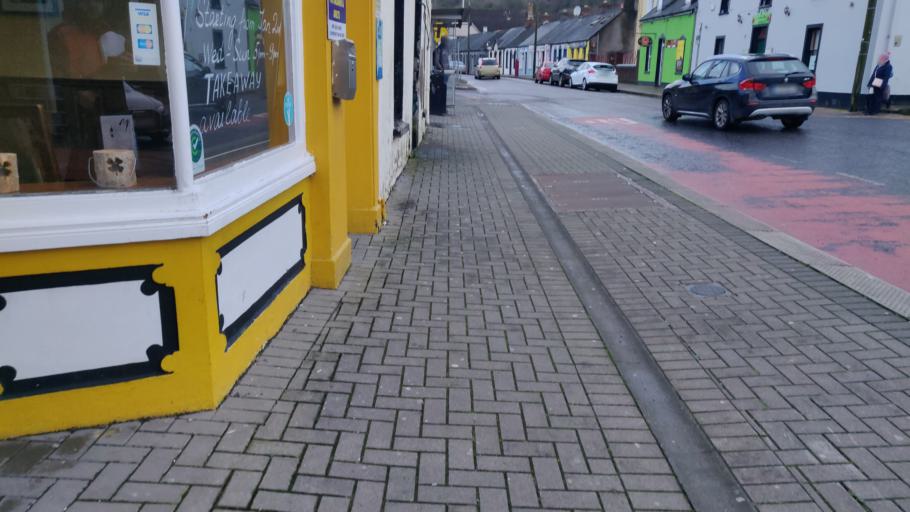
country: IE
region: Munster
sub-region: County Cork
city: Cork
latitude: 51.8771
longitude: -8.4357
